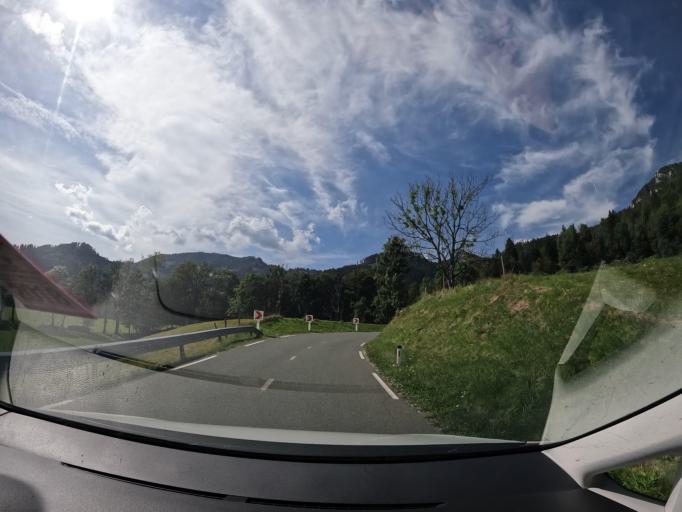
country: AT
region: Carinthia
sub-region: Politischer Bezirk Feldkirchen
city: Glanegg
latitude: 46.7419
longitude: 14.1727
